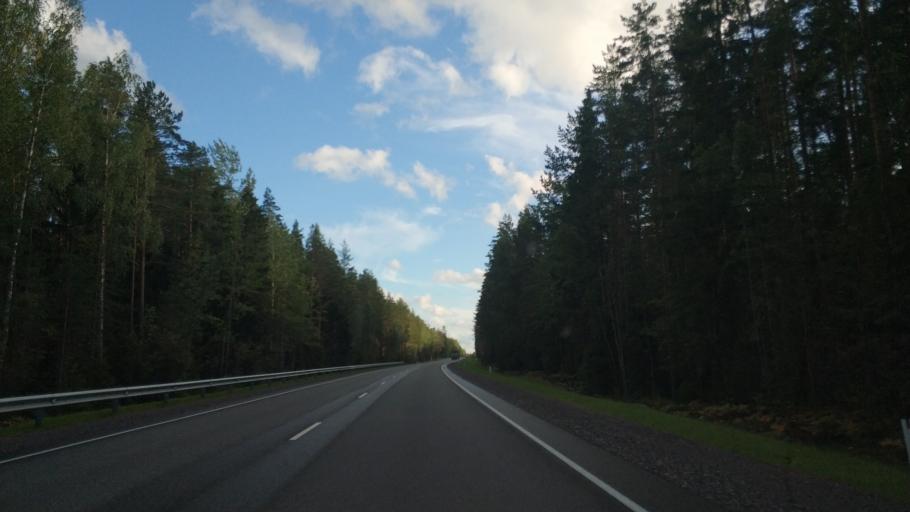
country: RU
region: Leningrad
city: Priozersk
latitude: 60.9066
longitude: 30.1600
